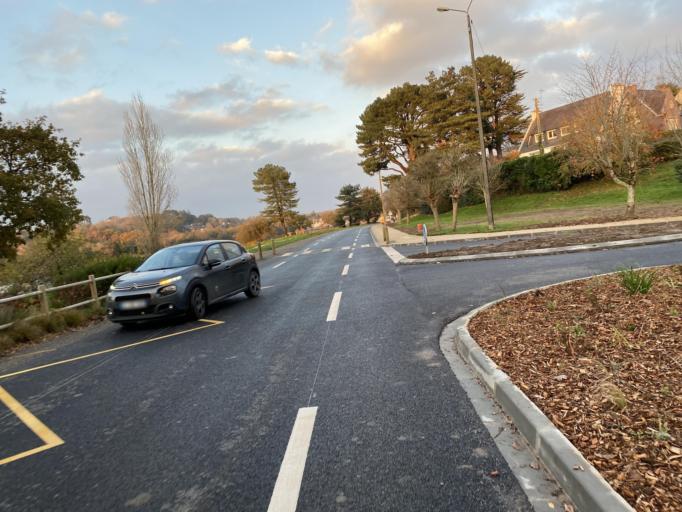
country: FR
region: Brittany
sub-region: Departement du Finistere
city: Daoulas
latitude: 48.3555
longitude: -4.2651
